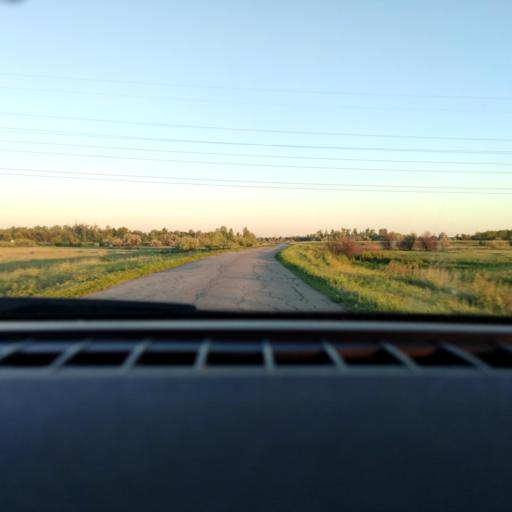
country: RU
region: Samara
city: Georgiyevka
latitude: 53.2664
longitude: 50.9613
